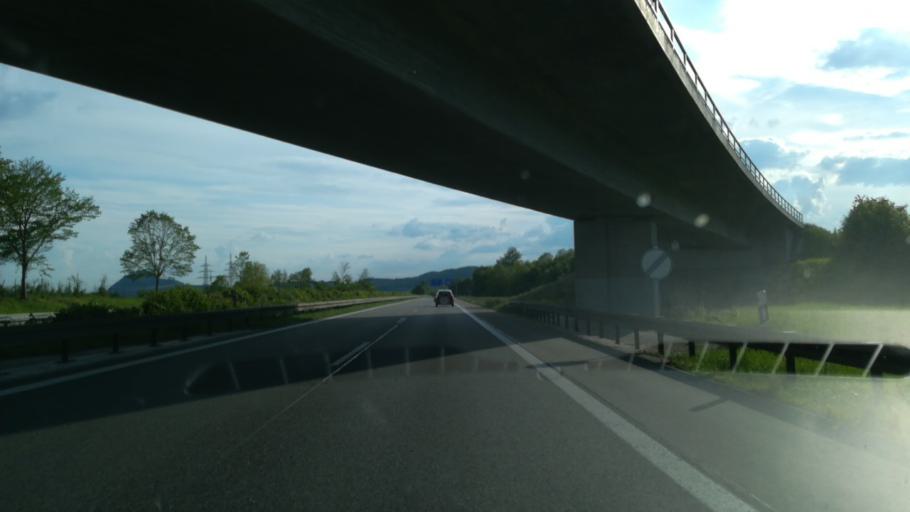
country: DE
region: Baden-Wuerttemberg
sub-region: Freiburg Region
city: Volkertshausen
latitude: 47.8087
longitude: 8.8614
